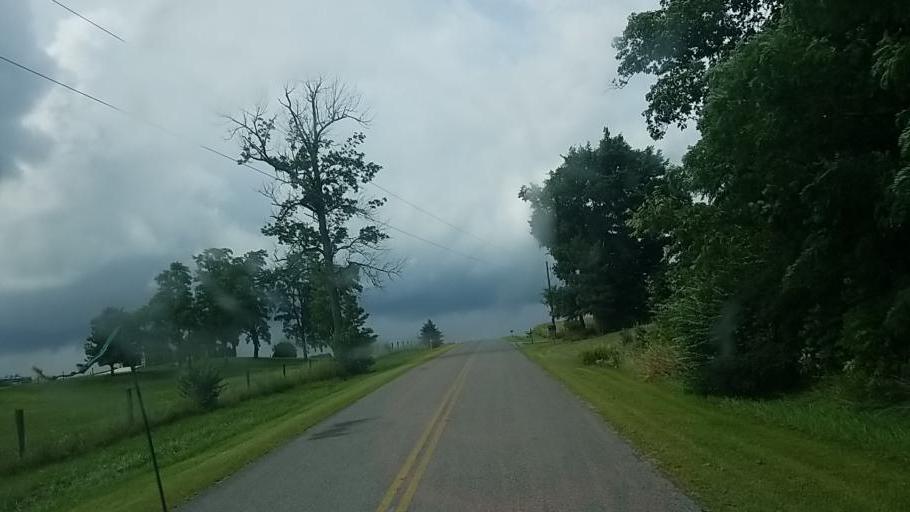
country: US
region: Ohio
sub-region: Champaign County
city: North Lewisburg
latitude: 40.2485
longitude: -83.6500
